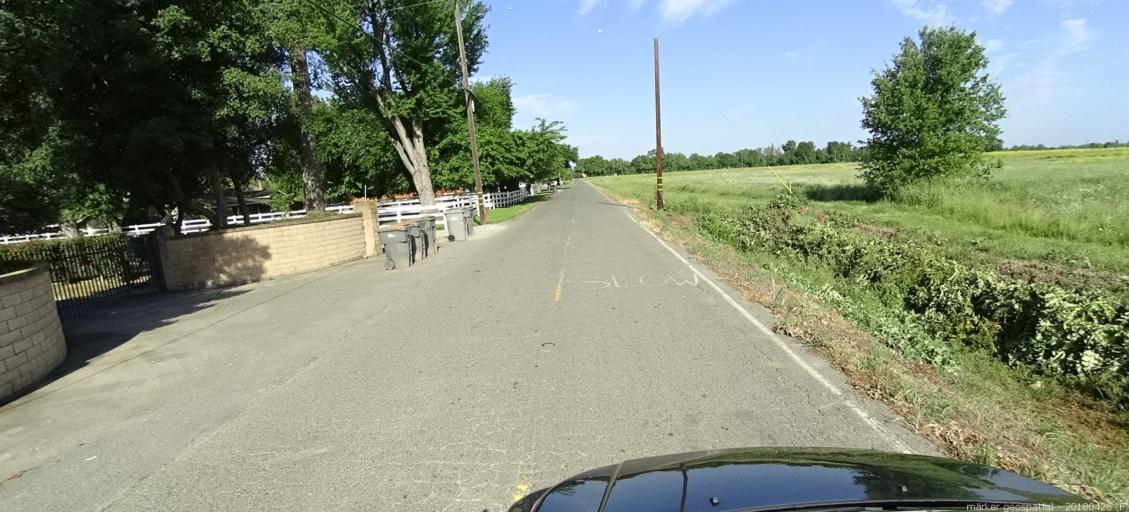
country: US
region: California
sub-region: Yolo County
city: West Sacramento
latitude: 38.5306
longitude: -121.5397
